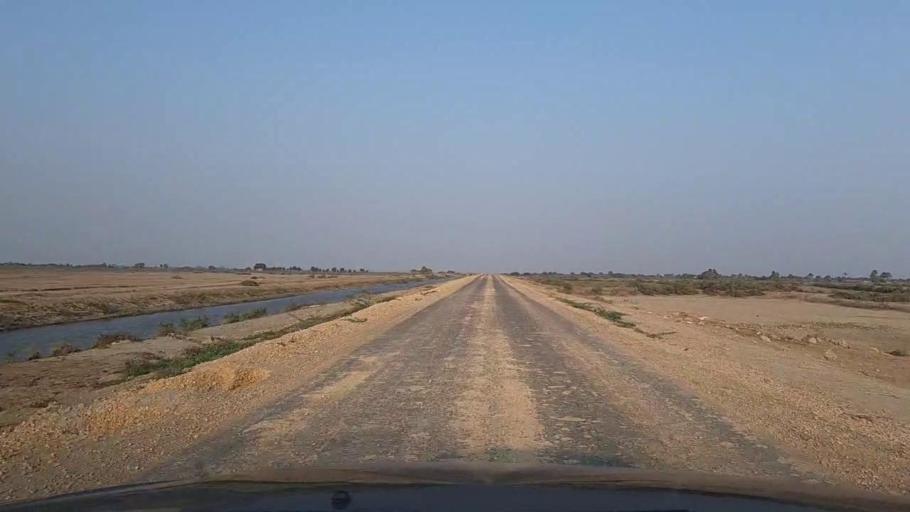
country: PK
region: Sindh
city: Mirpur Sakro
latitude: 24.4193
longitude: 67.7407
